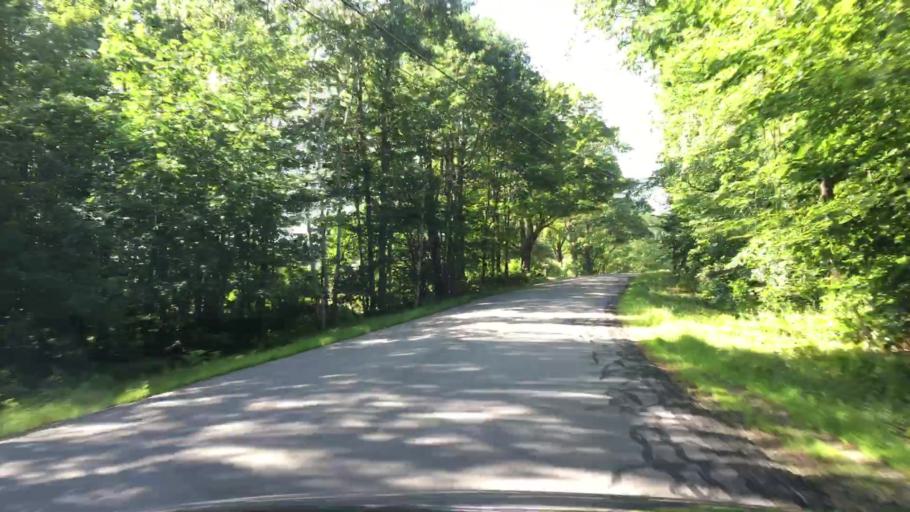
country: US
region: New Hampshire
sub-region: Grafton County
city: Ashland
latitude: 43.7131
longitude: -71.6299
